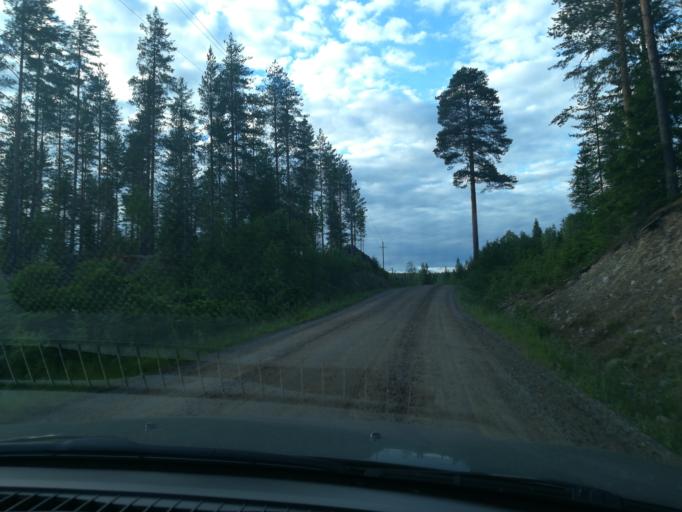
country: FI
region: Southern Savonia
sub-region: Mikkeli
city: Puumala
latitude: 61.5943
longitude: 28.1505
